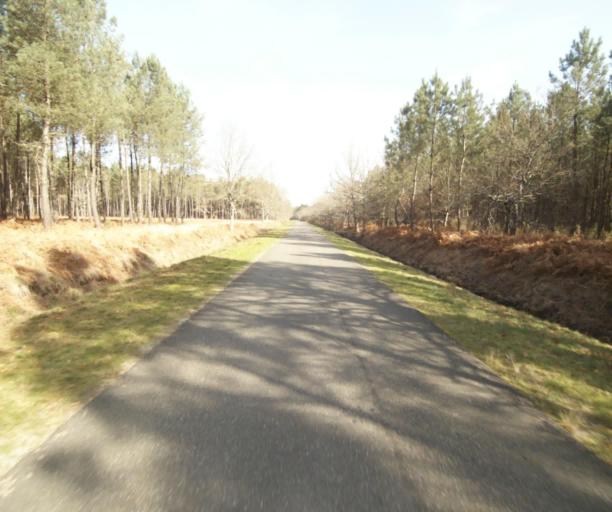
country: FR
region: Aquitaine
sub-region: Departement de la Gironde
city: Grignols
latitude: 44.1925
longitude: -0.1452
